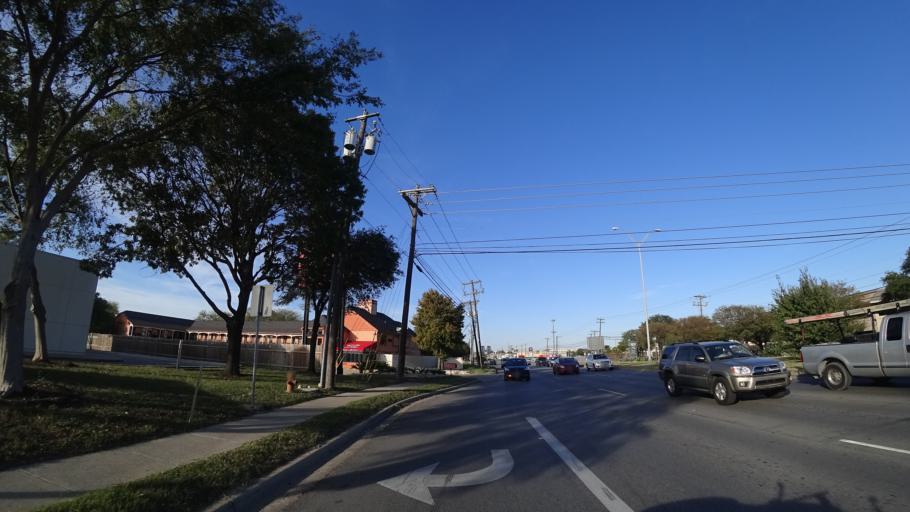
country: US
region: Texas
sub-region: Williamson County
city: Jollyville
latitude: 30.3743
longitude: -97.7264
